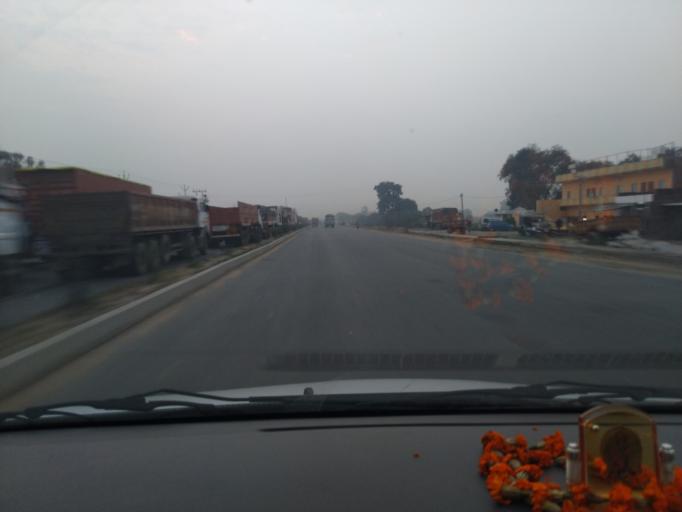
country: IN
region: Uttar Pradesh
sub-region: Ghazipur
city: Zamania
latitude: 25.2259
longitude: 83.4806
